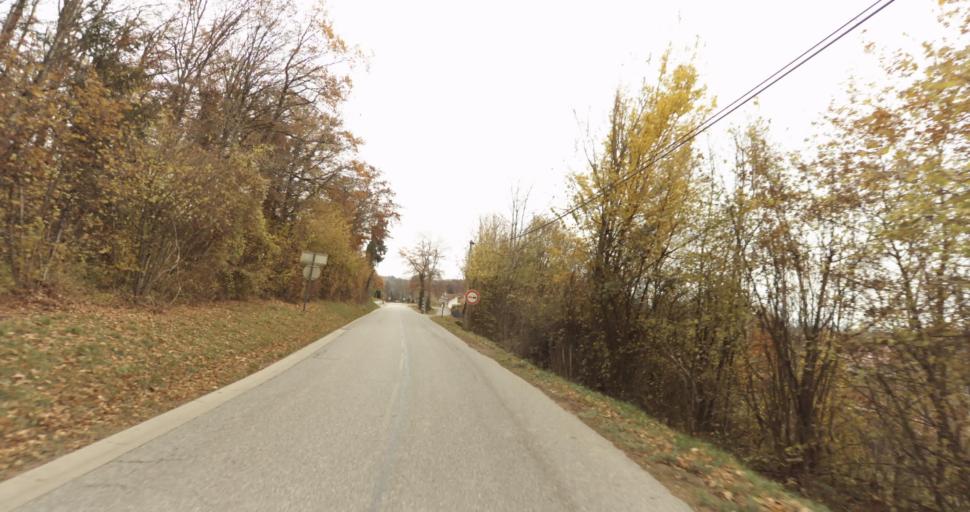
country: FR
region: Rhone-Alpes
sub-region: Departement de la Haute-Savoie
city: Saint-Martin-Bellevue
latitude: 45.9673
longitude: 6.1388
